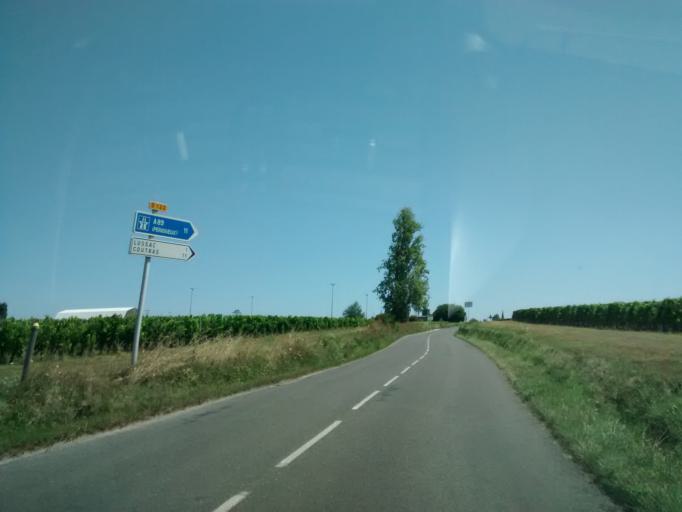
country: FR
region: Aquitaine
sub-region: Departement de la Gironde
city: Lussac
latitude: 44.9498
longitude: -0.1069
